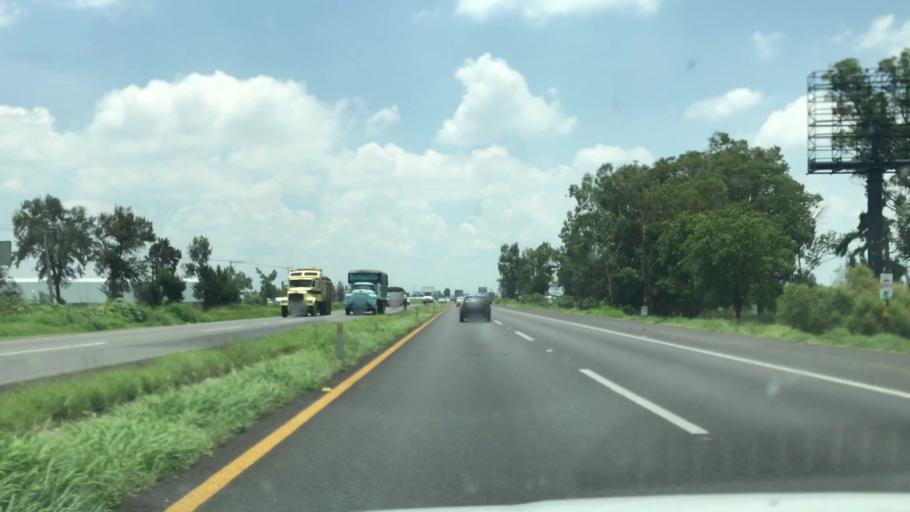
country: MX
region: Guanajuato
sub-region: Irapuato
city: San Jose de Bernalejo (El Guayabo)
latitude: 20.6073
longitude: -101.4113
